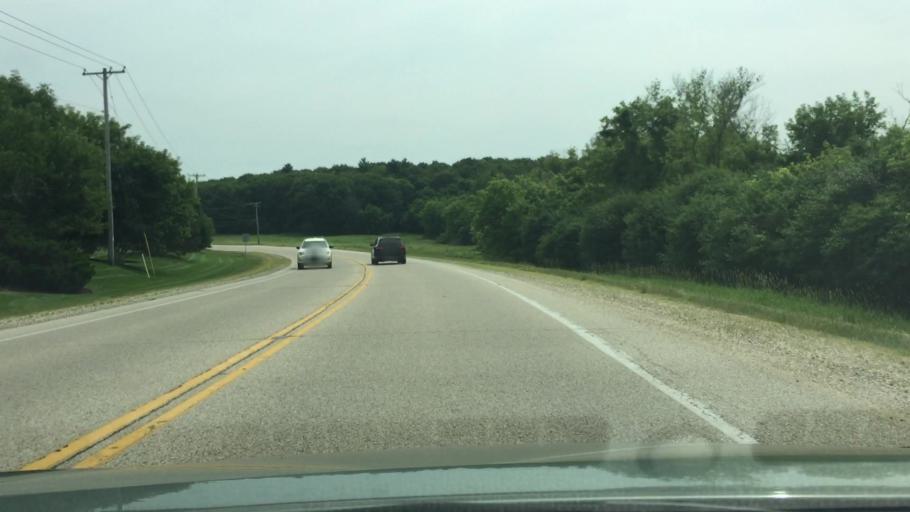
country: US
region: Wisconsin
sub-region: Waukesha County
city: Hartland
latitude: 43.0763
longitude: -88.3598
